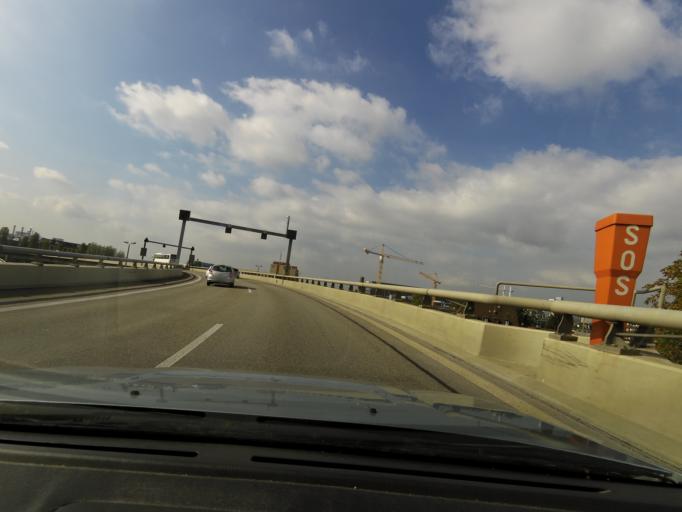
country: DE
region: Baden-Wuerttemberg
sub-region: Freiburg Region
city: Weil am Rhein
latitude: 47.5743
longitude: 7.6014
